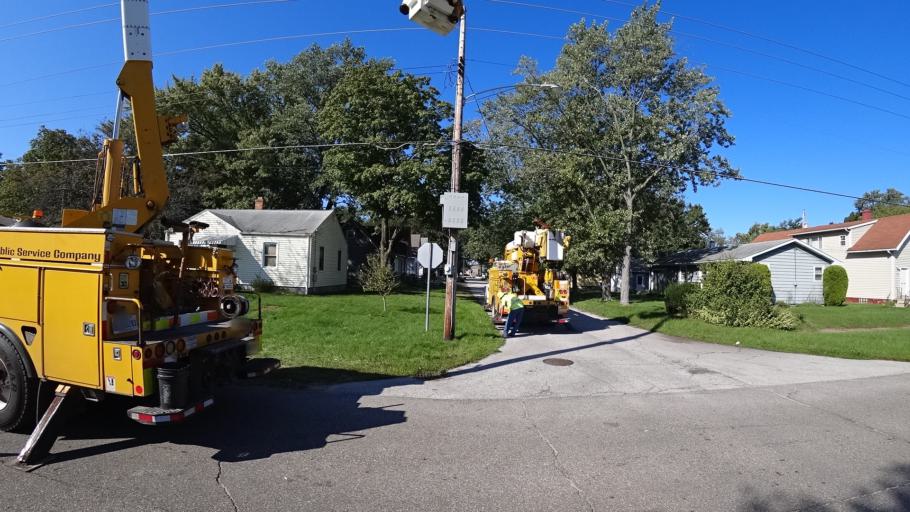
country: US
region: Indiana
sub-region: LaPorte County
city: Michigan City
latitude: 41.7046
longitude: -86.8921
